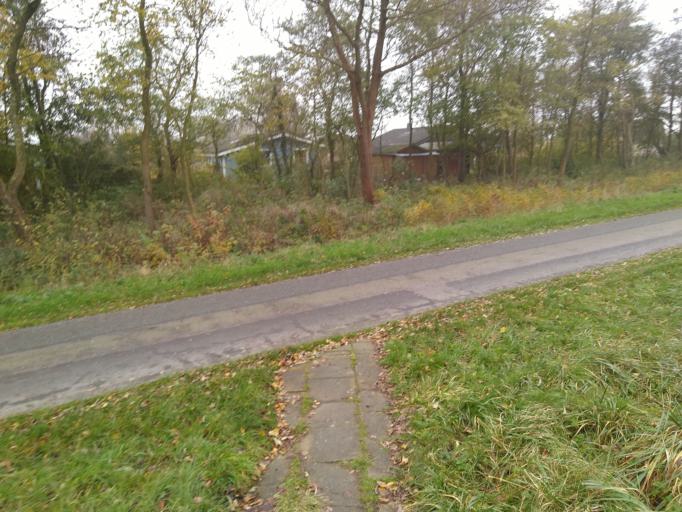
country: DE
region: Schleswig-Holstein
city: Simonsberg
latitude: 54.4537
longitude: 8.9685
